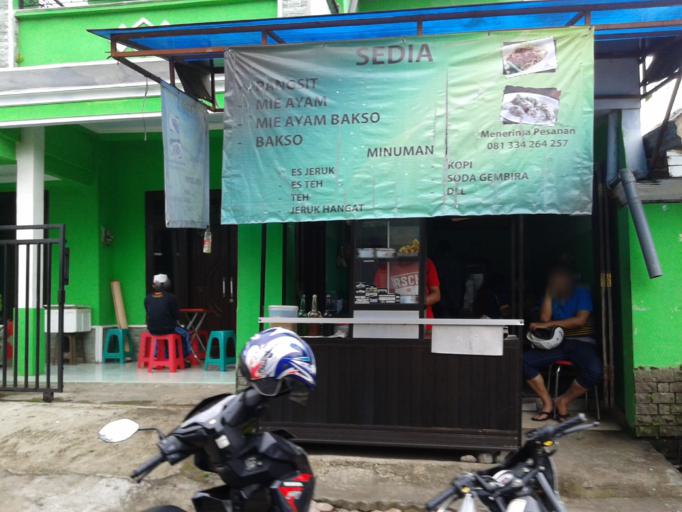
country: ID
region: East Java
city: Singosari
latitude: -7.8862
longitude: 112.6559
